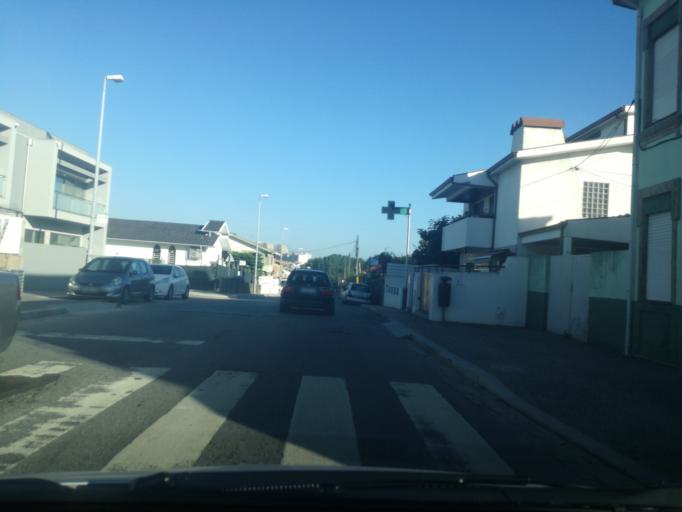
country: PT
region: Porto
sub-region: Maia
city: Milheiros
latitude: 41.2138
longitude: -8.5945
